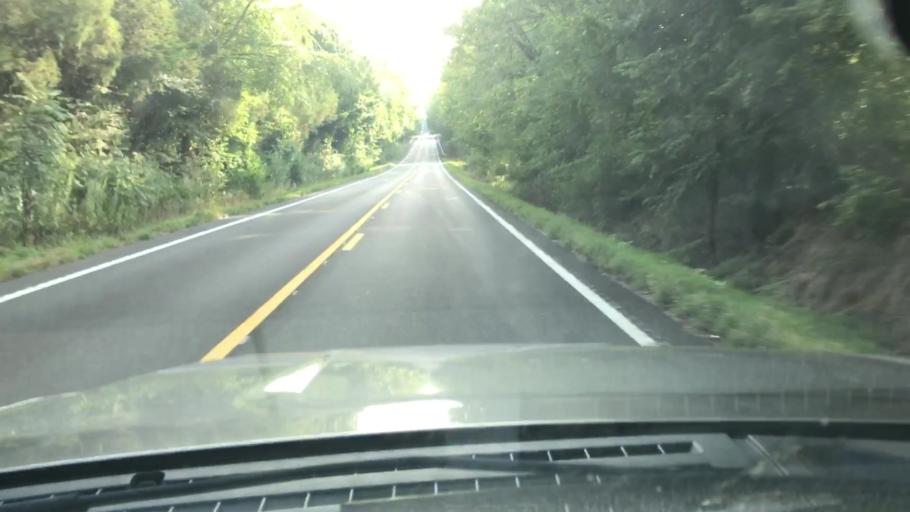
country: US
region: Tennessee
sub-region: Sumner County
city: Portland
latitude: 36.5574
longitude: -86.3916
